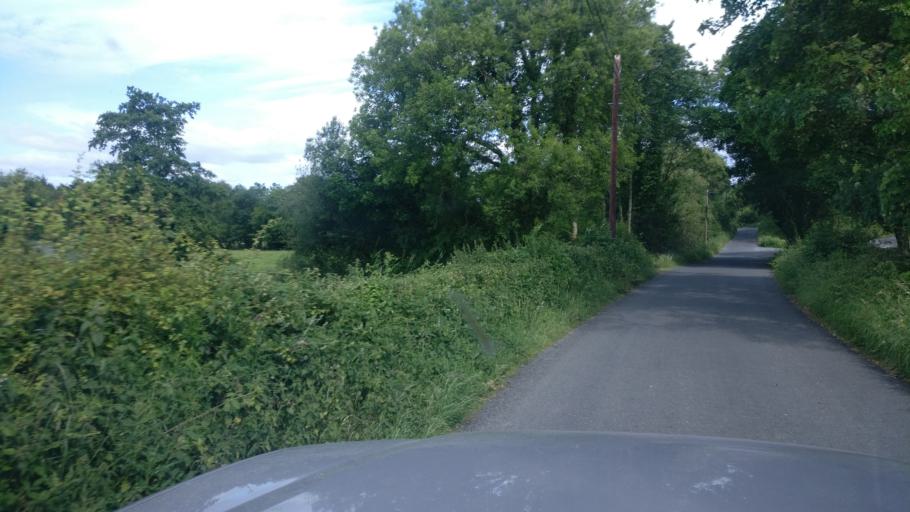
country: IE
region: Connaught
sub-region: County Galway
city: Gort
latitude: 53.0753
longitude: -8.7738
